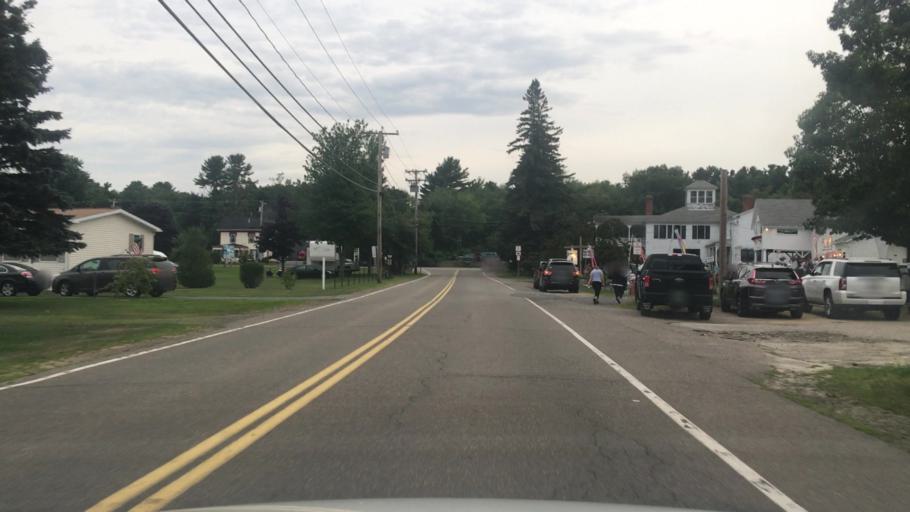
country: US
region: Maine
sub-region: York County
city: Wells Beach Station
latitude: 43.2912
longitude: -70.5886
